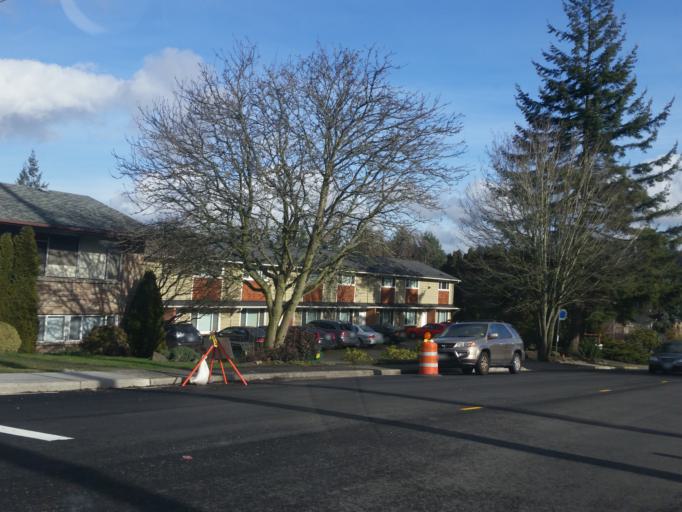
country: US
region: Washington
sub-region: Snohomish County
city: Esperance
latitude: 47.7924
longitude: -122.3354
